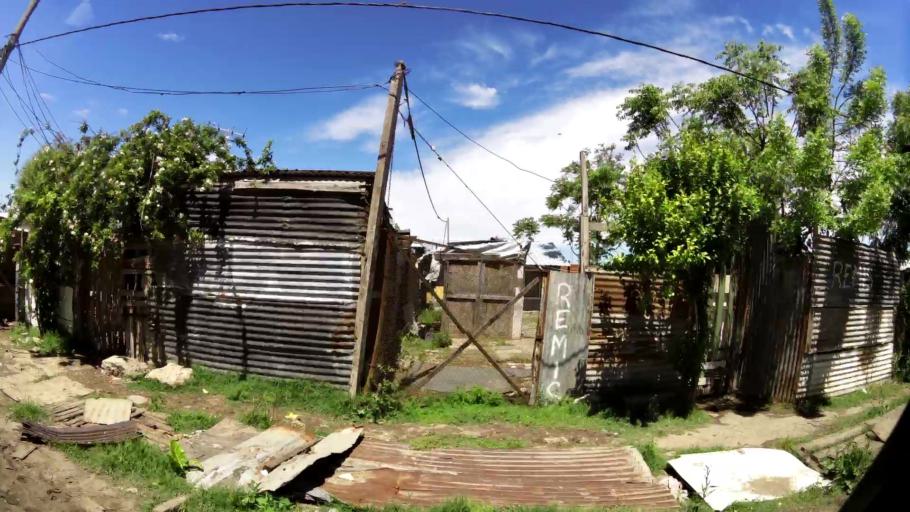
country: AR
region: Buenos Aires
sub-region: Partido de Quilmes
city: Quilmes
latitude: -34.7421
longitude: -58.3132
